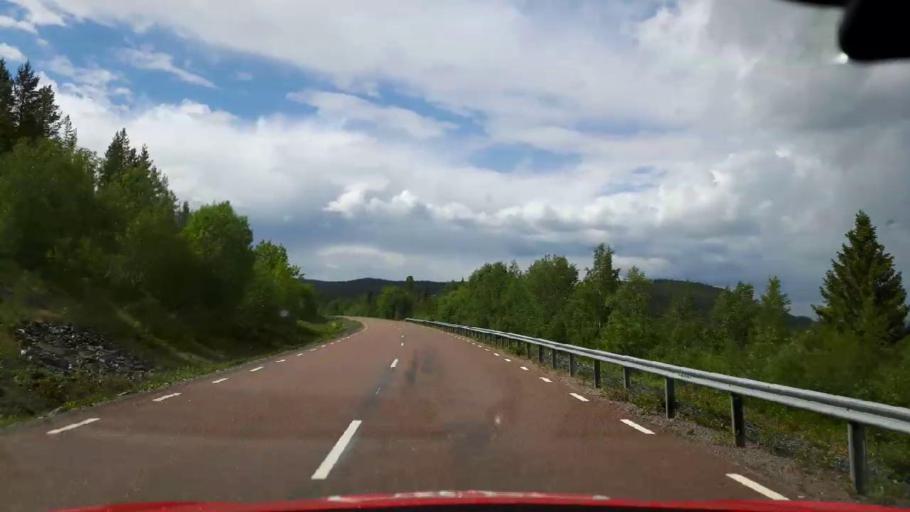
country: SE
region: Jaemtland
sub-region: Krokoms Kommun
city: Valla
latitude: 63.9000
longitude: 14.2402
